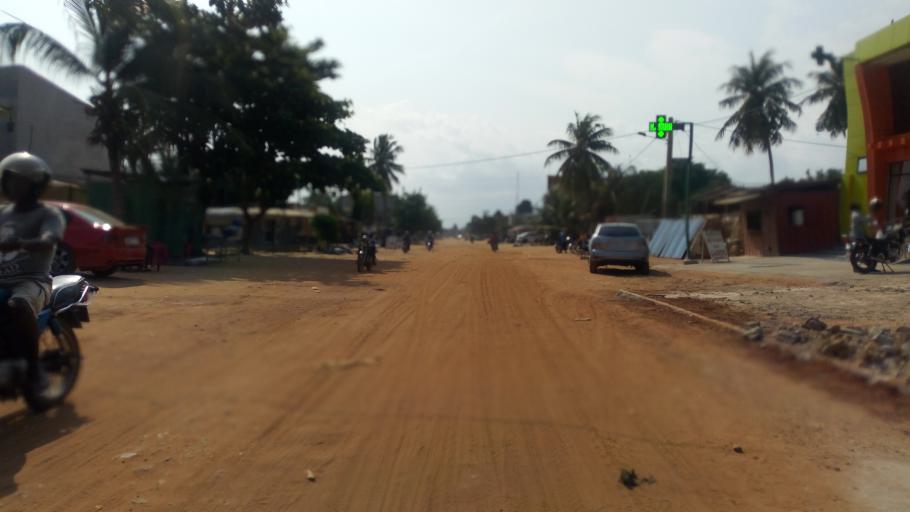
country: TG
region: Maritime
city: Lome
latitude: 6.1923
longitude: 1.1815
